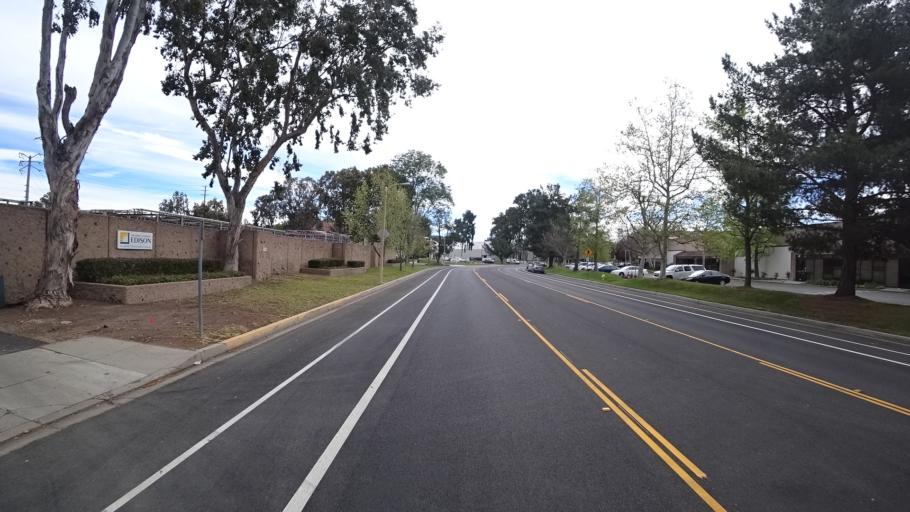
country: US
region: California
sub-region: Ventura County
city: Thousand Oaks
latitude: 34.1612
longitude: -118.8353
